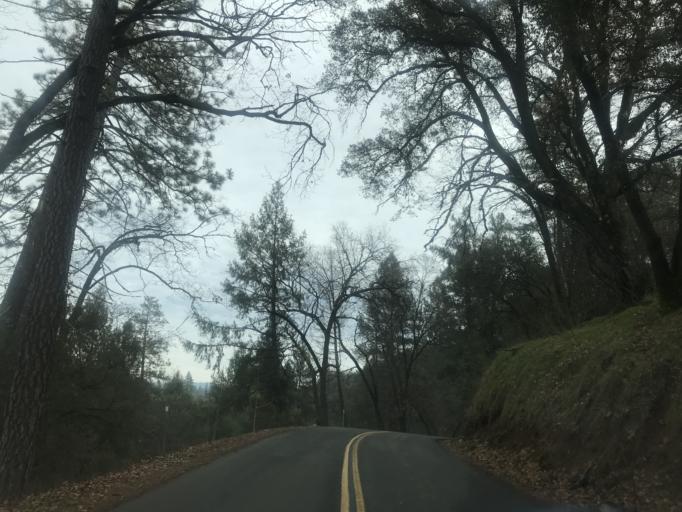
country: US
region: California
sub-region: El Dorado County
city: Placerville
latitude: 38.7288
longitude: -120.8172
